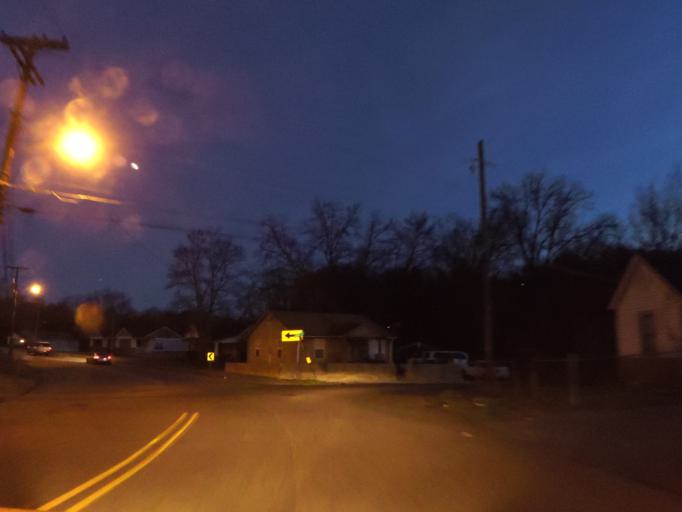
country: US
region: Tennessee
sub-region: Knox County
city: Knoxville
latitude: 35.9807
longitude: -83.8908
